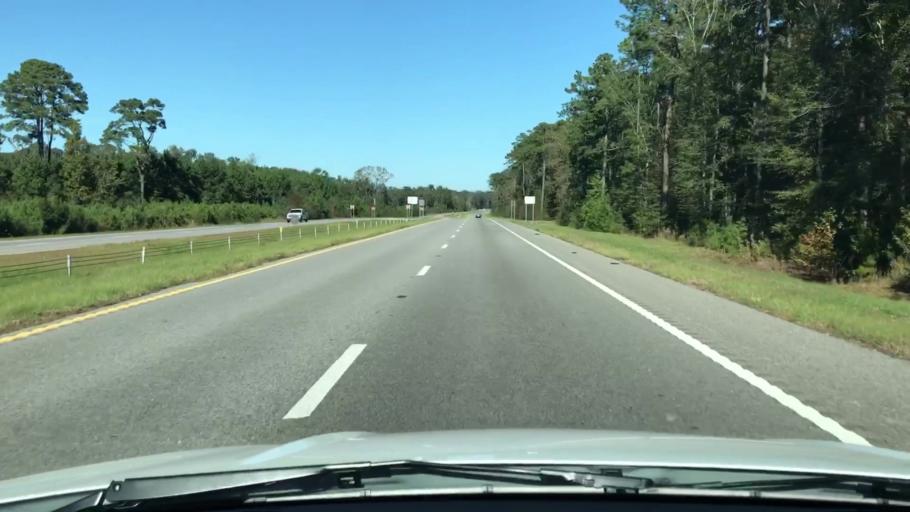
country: US
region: South Carolina
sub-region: Colleton County
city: Walterboro
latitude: 32.7156
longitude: -80.6053
